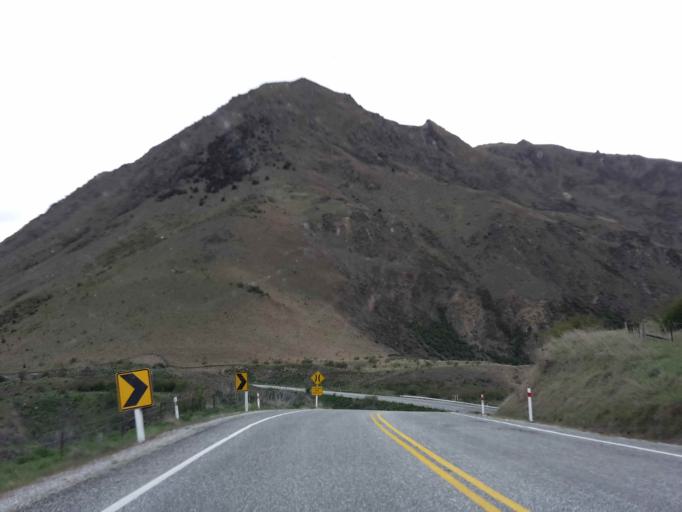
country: NZ
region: Otago
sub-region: Queenstown-Lakes District
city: Wanaka
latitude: -44.6095
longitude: 169.5403
